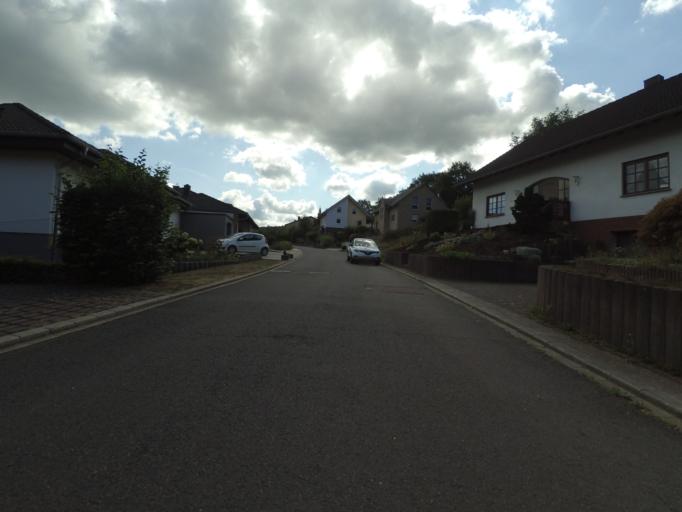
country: DE
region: Rheinland-Pfalz
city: Trassem
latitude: 49.5816
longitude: 6.5224
